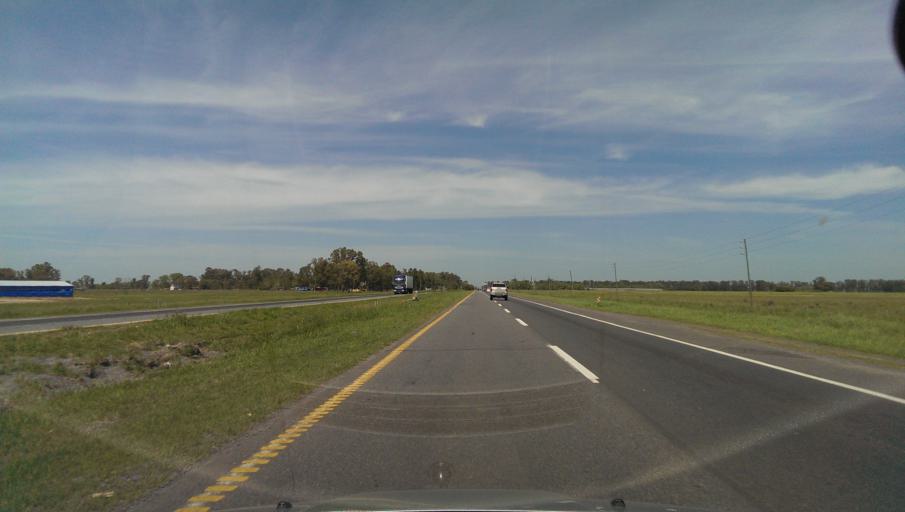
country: AR
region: Buenos Aires
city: Canuelas
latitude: -35.1137
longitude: -58.7358
